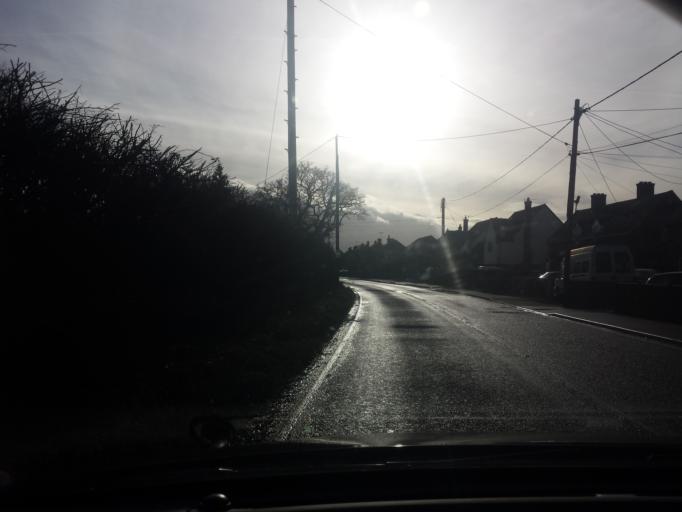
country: GB
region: England
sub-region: Essex
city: Great Bentley
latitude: 51.8732
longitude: 1.0353
